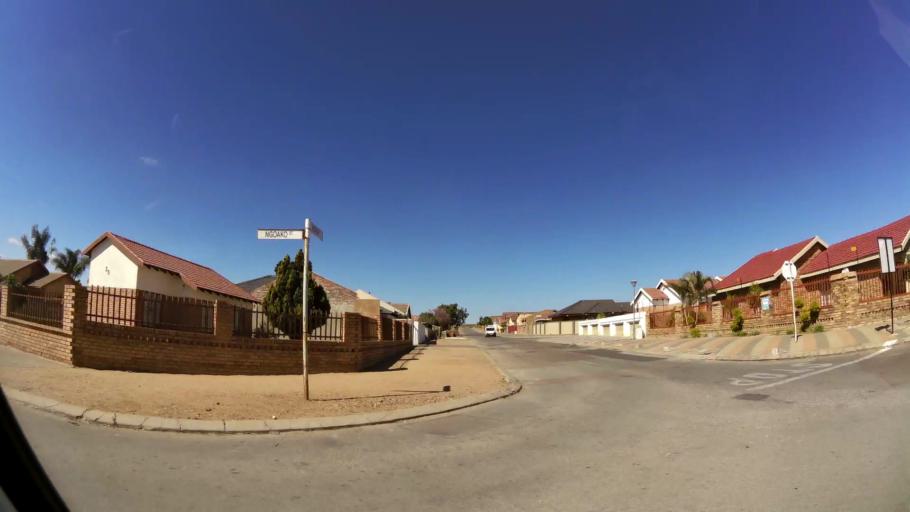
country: ZA
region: Limpopo
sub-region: Capricorn District Municipality
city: Polokwane
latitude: -23.8736
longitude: 29.4133
